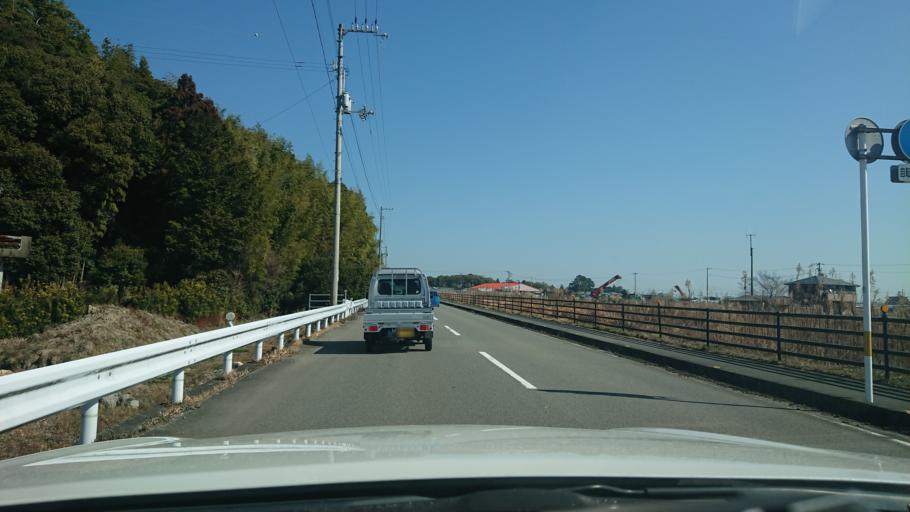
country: JP
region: Tokushima
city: Komatsushimacho
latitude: 33.9722
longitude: 134.6003
